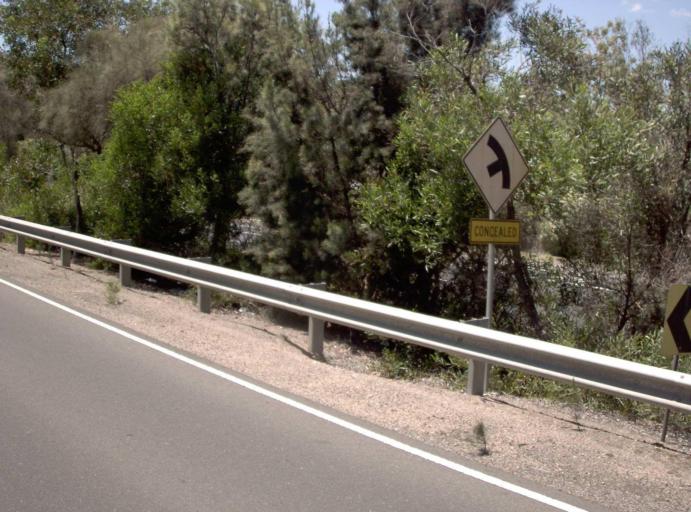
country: AU
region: Victoria
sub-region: Mornington Peninsula
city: Mount Eliza
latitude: -38.1849
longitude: 145.0968
